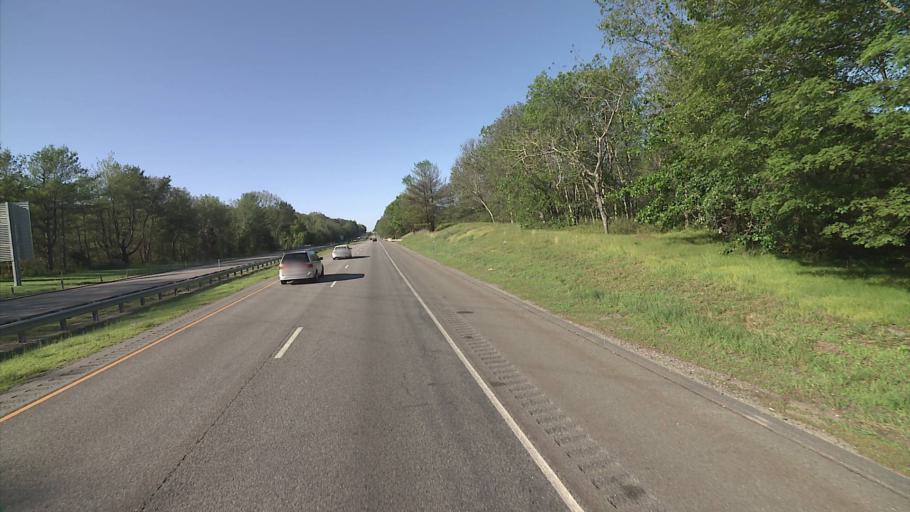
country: US
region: Connecticut
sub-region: Windham County
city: Moosup
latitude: 41.7116
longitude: -71.8969
